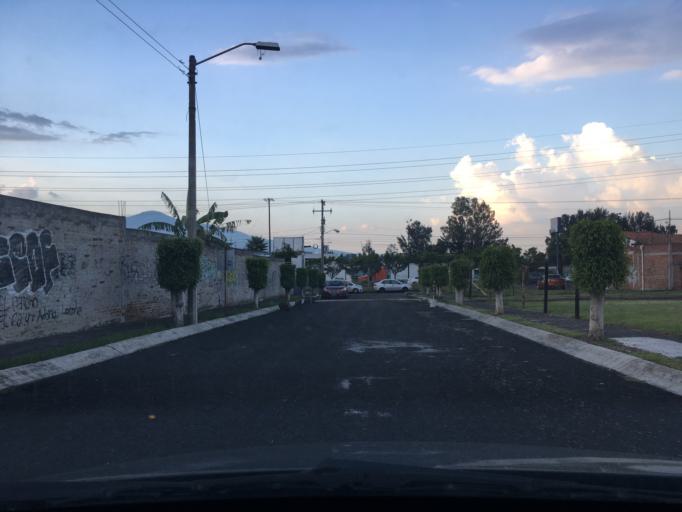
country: MX
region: Michoacan
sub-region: Morelia
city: Morelos
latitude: 19.6761
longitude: -101.2283
